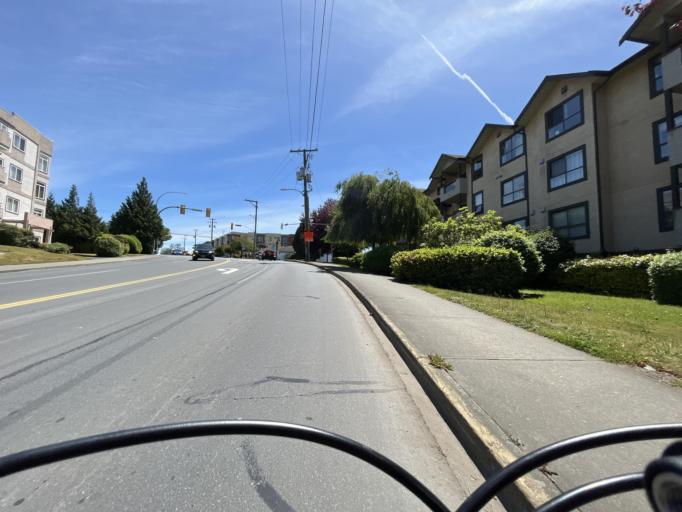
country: CA
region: British Columbia
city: Victoria
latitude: 48.4441
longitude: -123.3912
